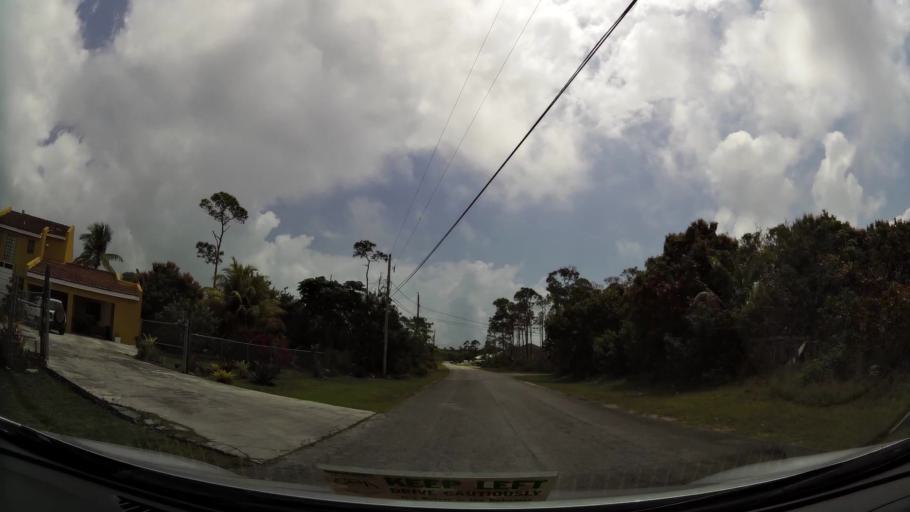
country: BS
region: Freeport
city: Lucaya
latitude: 26.5239
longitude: -78.6521
